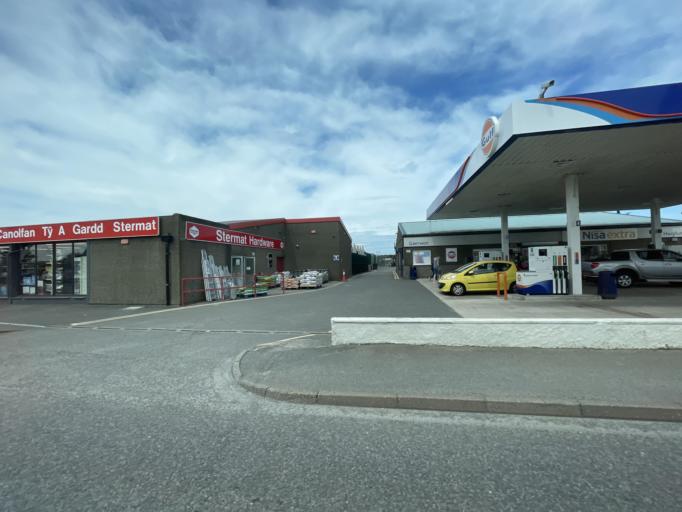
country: GB
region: Wales
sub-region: Anglesey
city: Gaerwen
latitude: 53.2225
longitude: -4.2666
